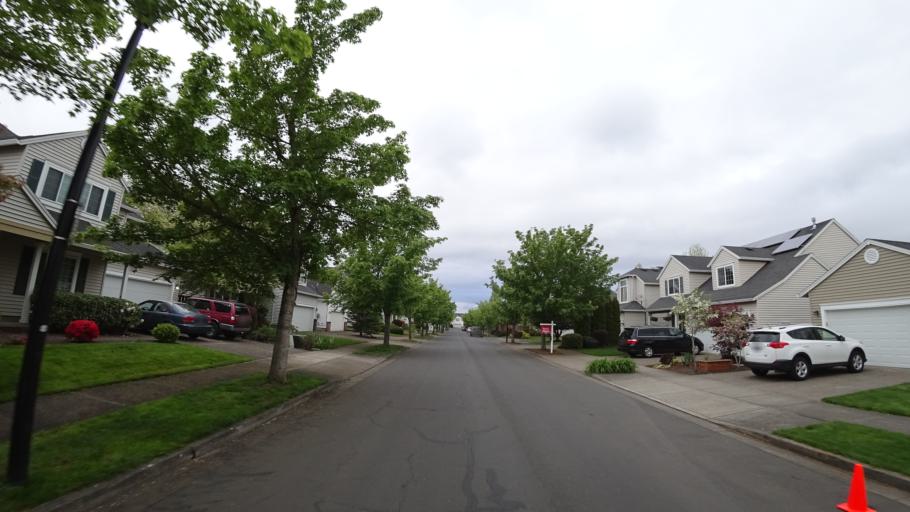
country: US
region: Oregon
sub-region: Washington County
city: Hillsboro
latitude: 45.5403
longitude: -122.9701
